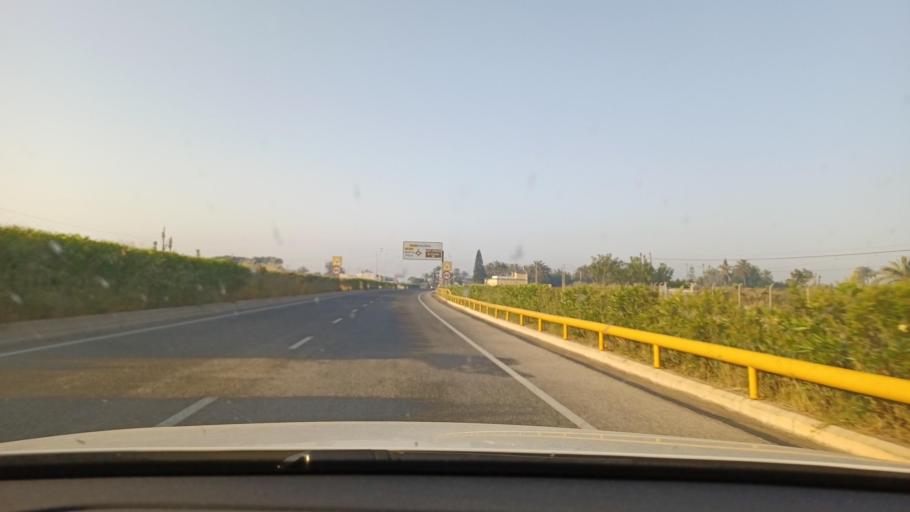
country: ES
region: Valencia
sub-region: Provincia de Alicante
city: Elche
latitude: 38.1904
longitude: -0.7011
